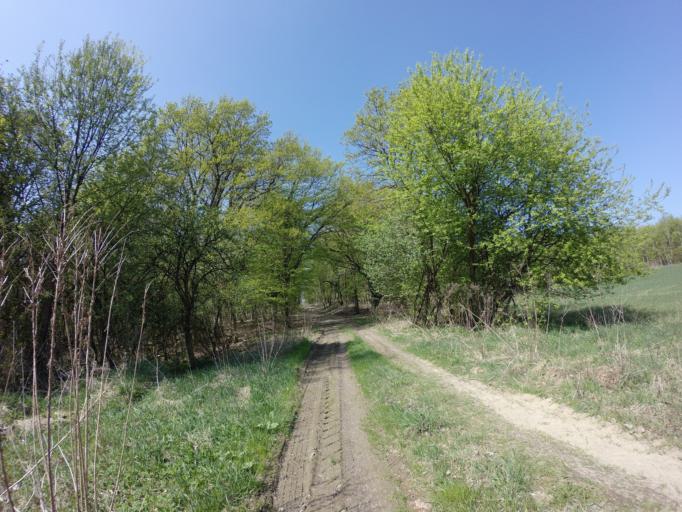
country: PL
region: West Pomeranian Voivodeship
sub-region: Powiat choszczenski
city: Choszczno
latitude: 53.1933
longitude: 15.3685
